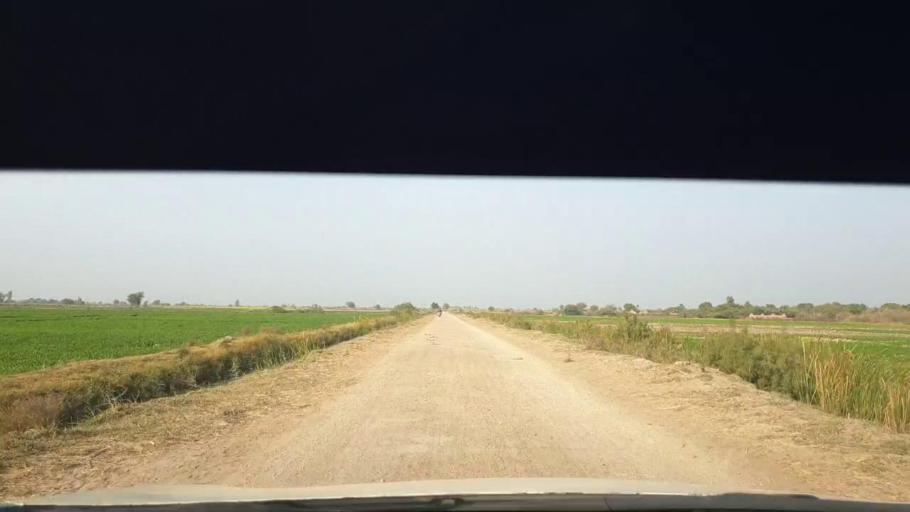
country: PK
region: Sindh
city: Berani
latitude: 25.7556
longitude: 68.9407
